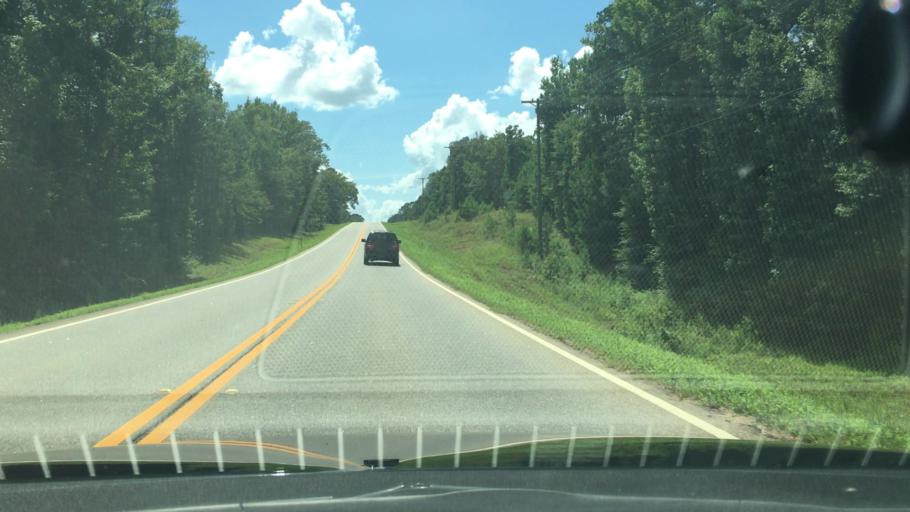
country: US
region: Georgia
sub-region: Putnam County
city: Eatonton
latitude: 33.3088
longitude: -83.4709
